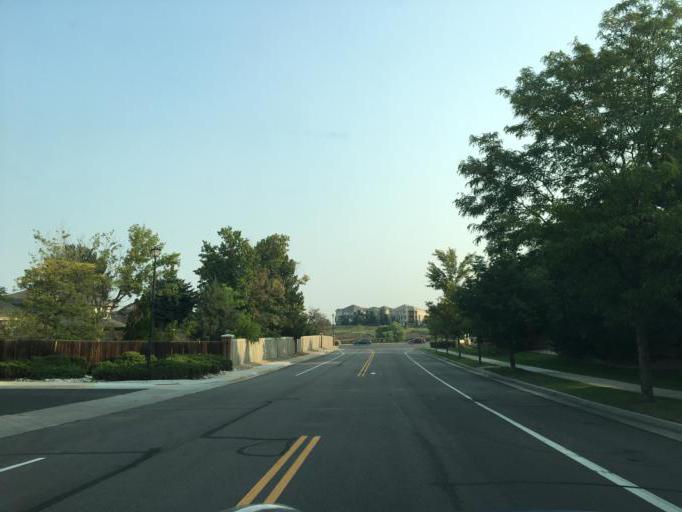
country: US
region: Colorado
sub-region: Adams County
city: Westminster
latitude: 39.8838
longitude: -105.0486
